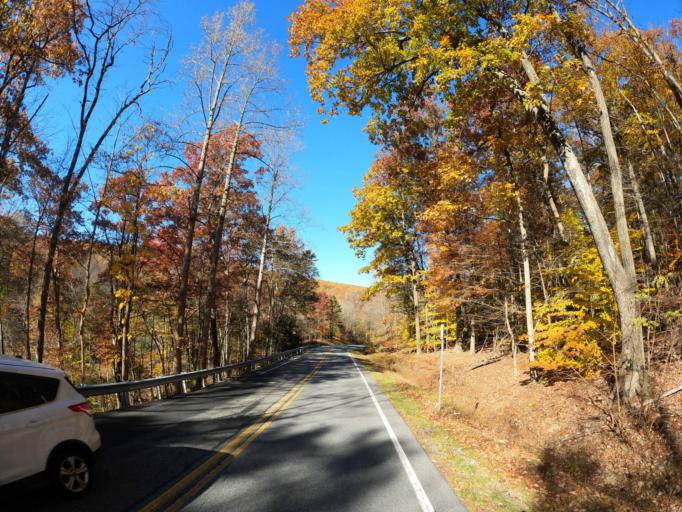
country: US
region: Maryland
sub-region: Frederick County
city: Thurmont
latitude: 39.6295
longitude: -77.4548
